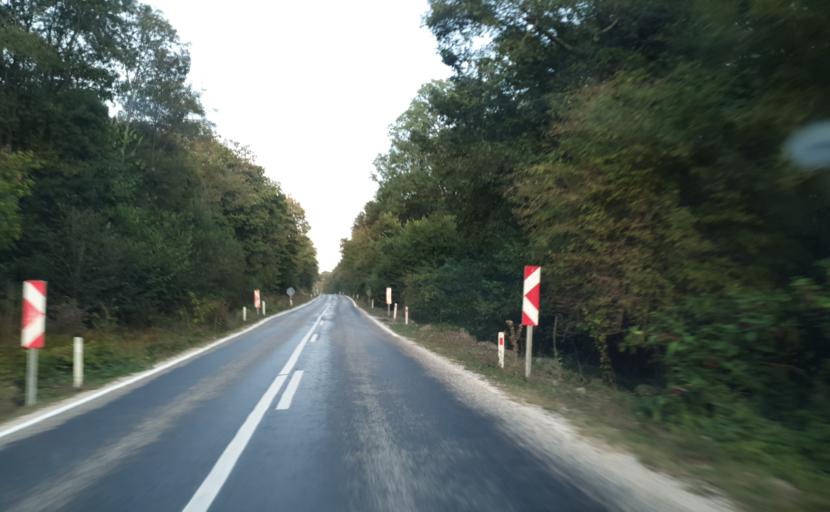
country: TR
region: Kirklareli
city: Igneada
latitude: 41.8714
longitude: 27.9280
